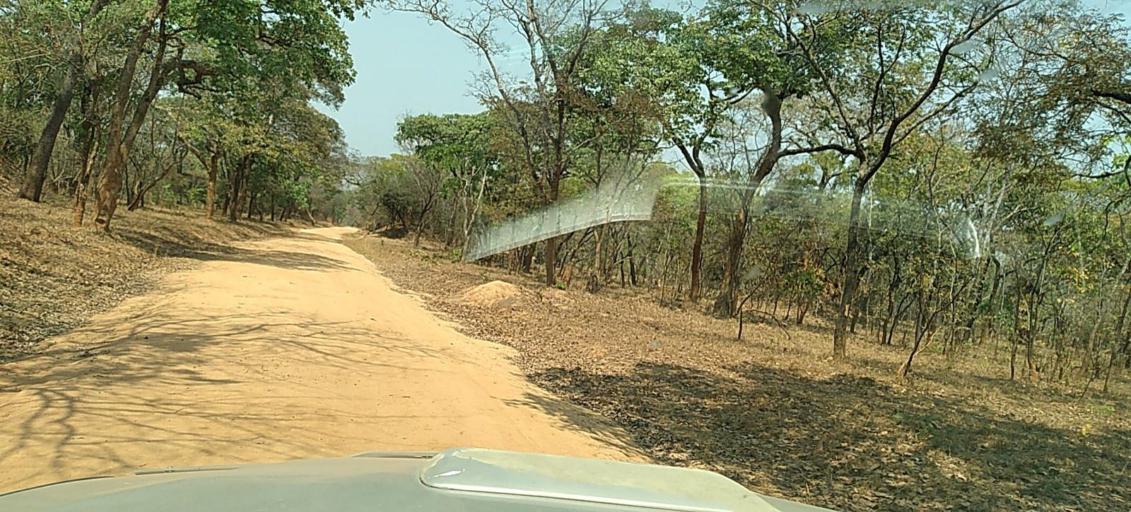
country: ZM
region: North-Western
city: Kasempa
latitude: -13.6651
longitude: 26.2825
